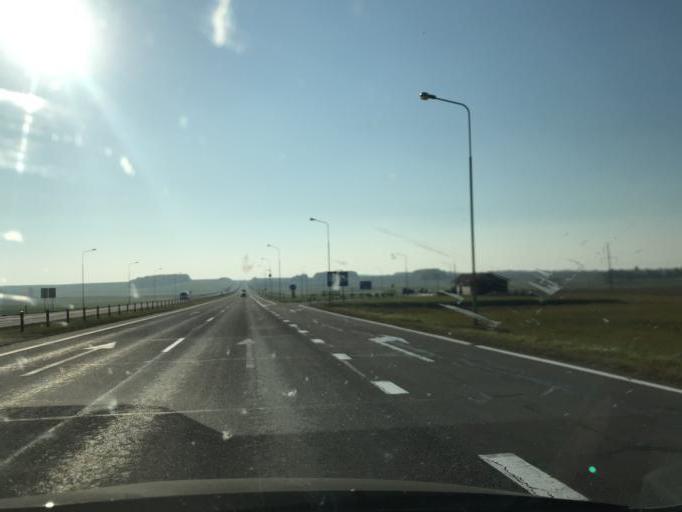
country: BY
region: Minsk
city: Haradzyeya
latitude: 53.3428
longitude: 26.4441
